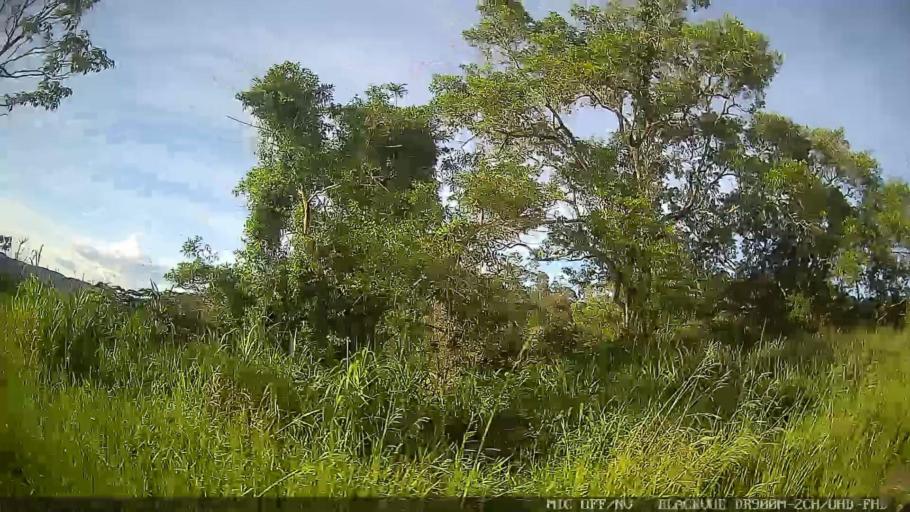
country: BR
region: Sao Paulo
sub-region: Mogi das Cruzes
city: Mogi das Cruzes
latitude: -23.5207
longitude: -46.1475
